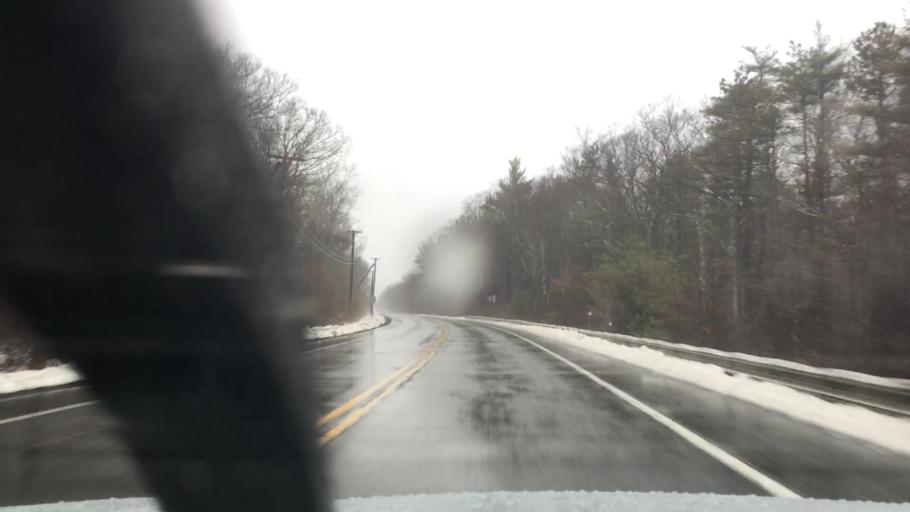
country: US
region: Massachusetts
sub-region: Hampshire County
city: Pelham
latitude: 42.3811
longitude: -72.4010
